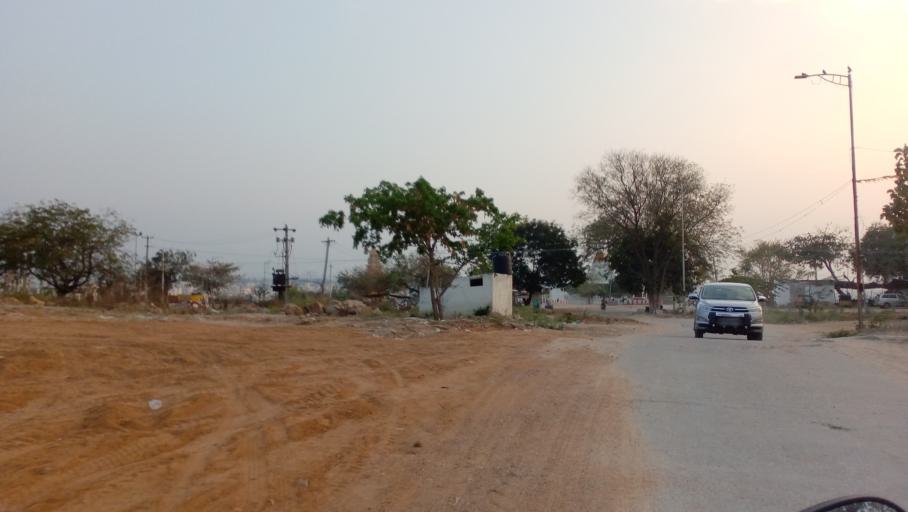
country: IN
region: Telangana
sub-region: Medak
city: Serilingampalle
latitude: 17.5202
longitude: 78.3070
